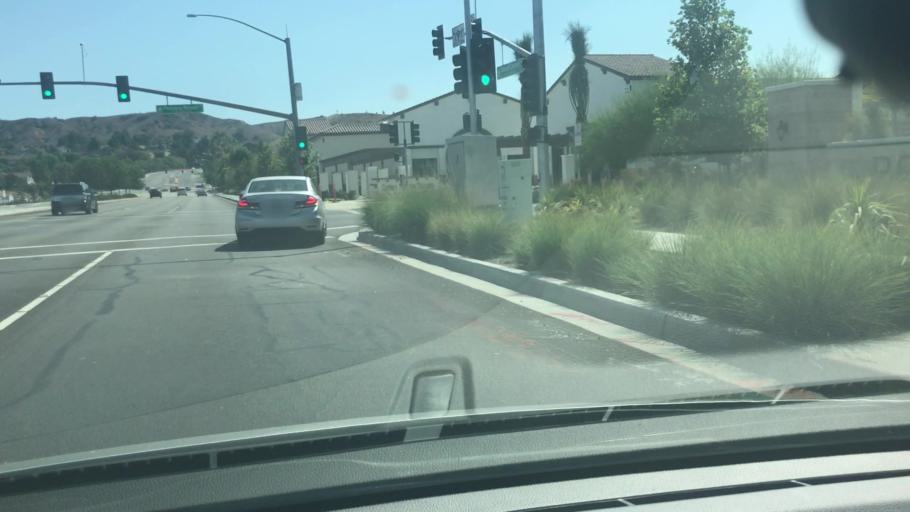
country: US
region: California
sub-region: San Bernardino County
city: Los Serranos
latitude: 33.9649
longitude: -117.6921
